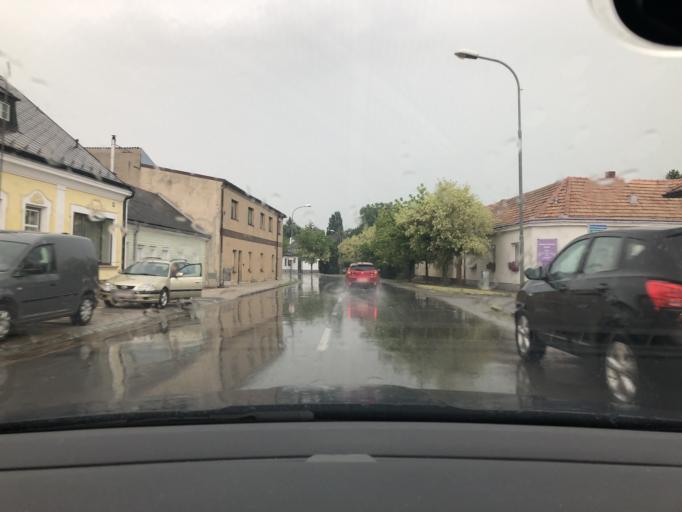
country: AT
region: Lower Austria
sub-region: Politischer Bezirk Ganserndorf
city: Marchegg
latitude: 48.2766
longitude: 16.9101
